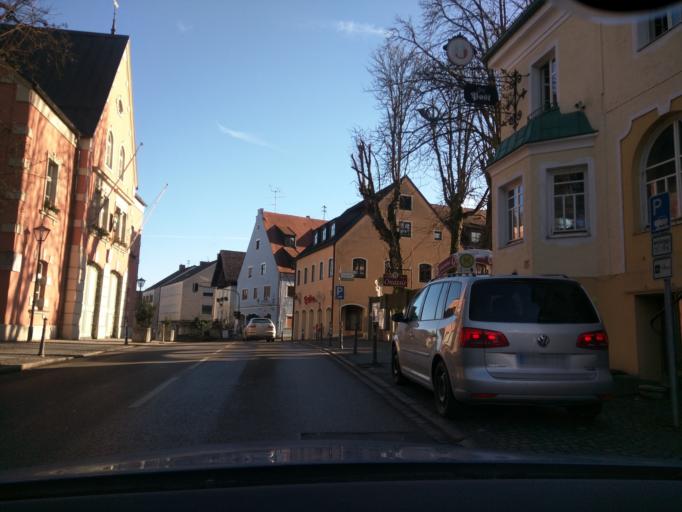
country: DE
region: Bavaria
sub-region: Upper Bavaria
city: Au in der Hallertau
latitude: 48.5576
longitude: 11.7422
